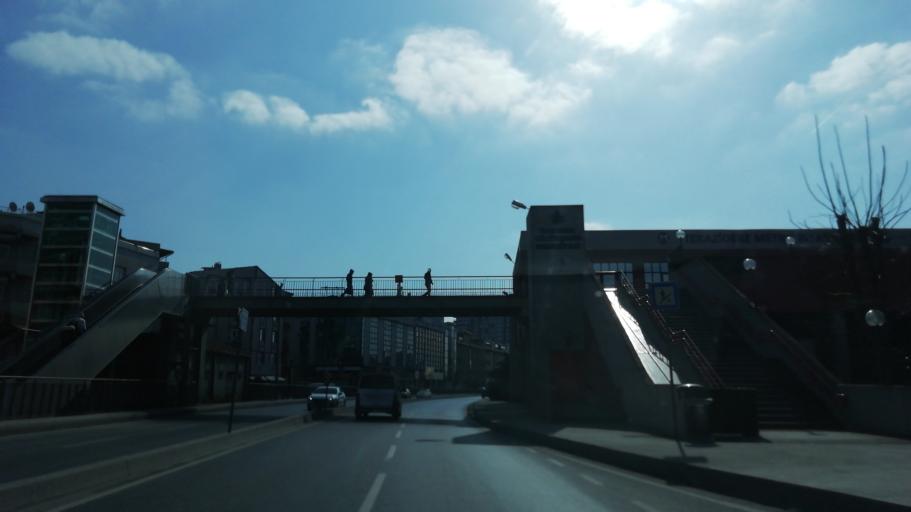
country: TR
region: Istanbul
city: merter keresteciler
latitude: 41.0310
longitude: 28.8977
